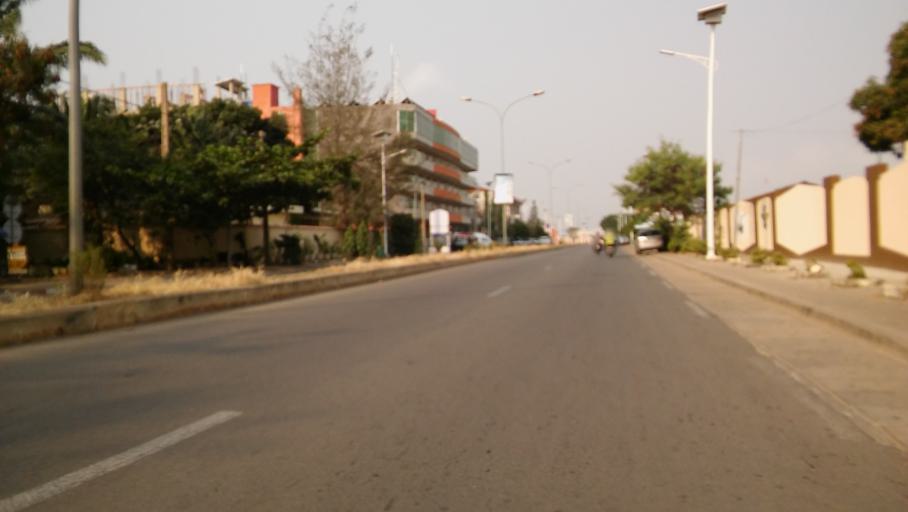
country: BJ
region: Littoral
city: Cotonou
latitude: 6.3539
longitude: 2.3892
